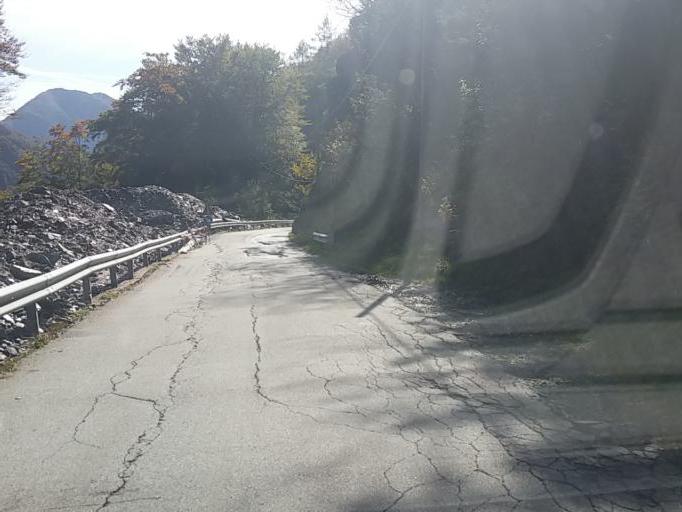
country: IT
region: Piedmont
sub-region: Provincia Verbano-Cusio-Ossola
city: Villette
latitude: 46.1094
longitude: 8.5325
